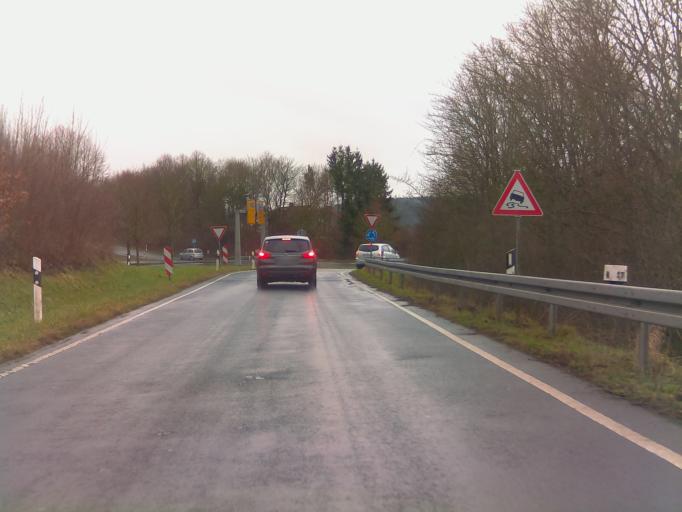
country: DE
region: Hesse
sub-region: Regierungsbezirk Kassel
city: Eichenzell
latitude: 50.5223
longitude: 9.6838
